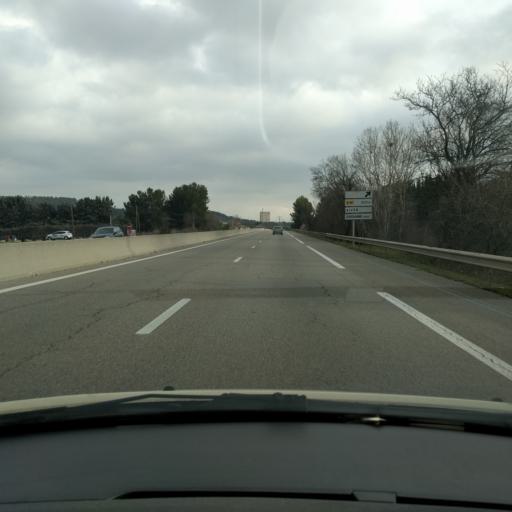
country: FR
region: Provence-Alpes-Cote d'Azur
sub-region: Departement des Bouches-du-Rhone
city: Simiane-Collongue
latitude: 43.4433
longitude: 5.4372
